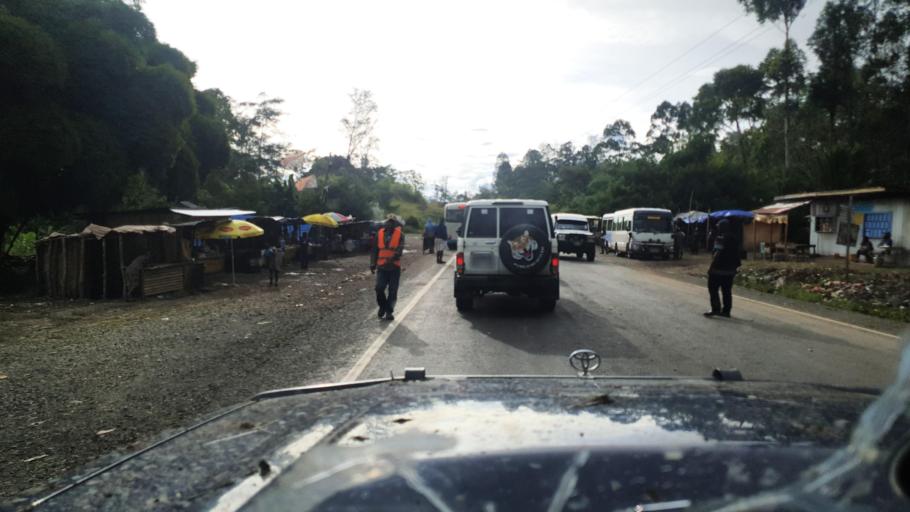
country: PG
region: Jiwaka
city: Minj
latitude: -5.9308
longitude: 144.7994
